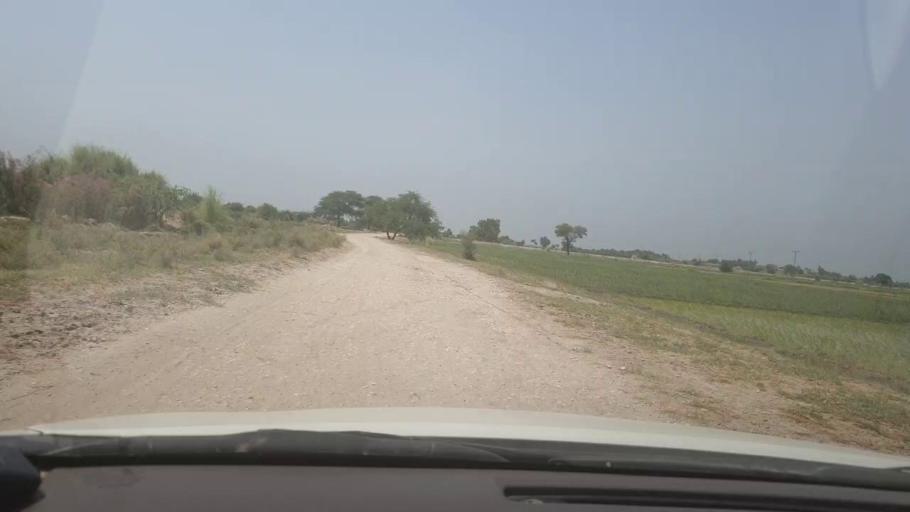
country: PK
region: Sindh
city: Shikarpur
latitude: 27.9398
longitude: 68.5743
